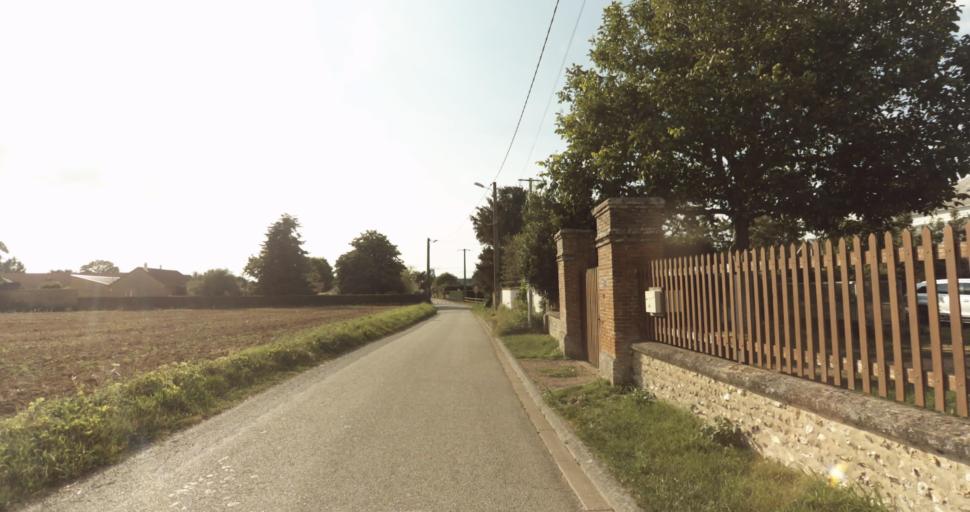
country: FR
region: Haute-Normandie
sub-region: Departement de l'Eure
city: La Couture-Boussey
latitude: 48.8953
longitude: 1.3641
